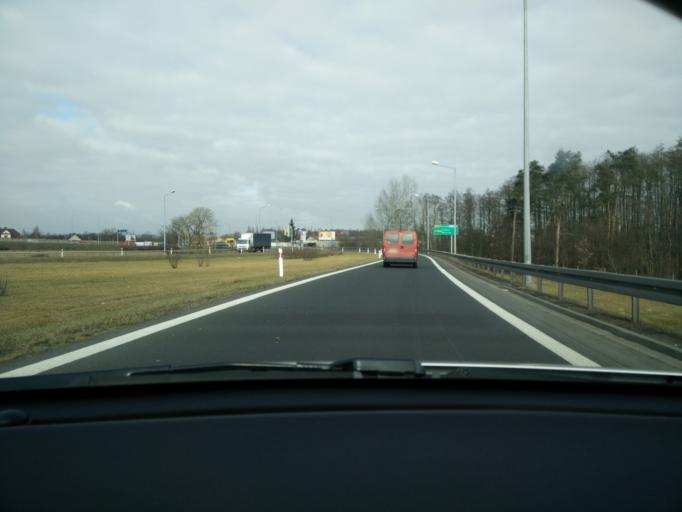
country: PL
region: Greater Poland Voivodeship
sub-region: Powiat poznanski
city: Lubon
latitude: 52.3541
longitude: 16.9058
